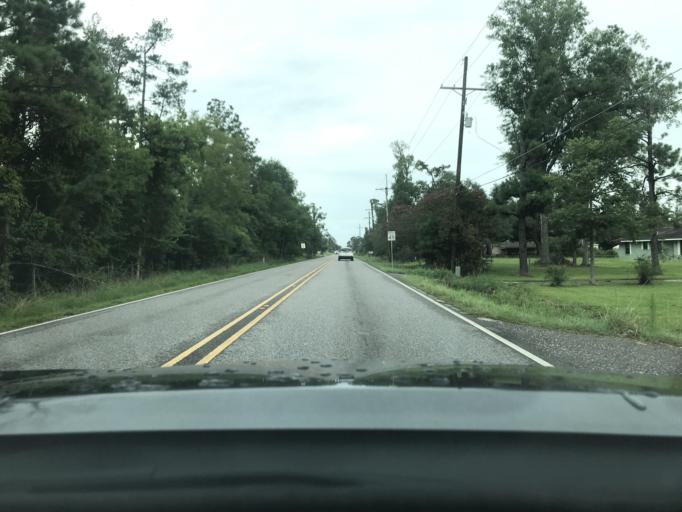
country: US
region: Louisiana
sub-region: Calcasieu Parish
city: Westlake
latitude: 30.2702
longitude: -93.2582
